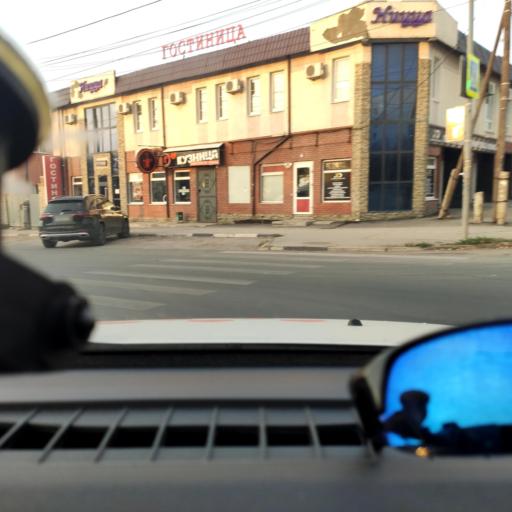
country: RU
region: Samara
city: Samara
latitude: 53.1849
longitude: 50.1915
